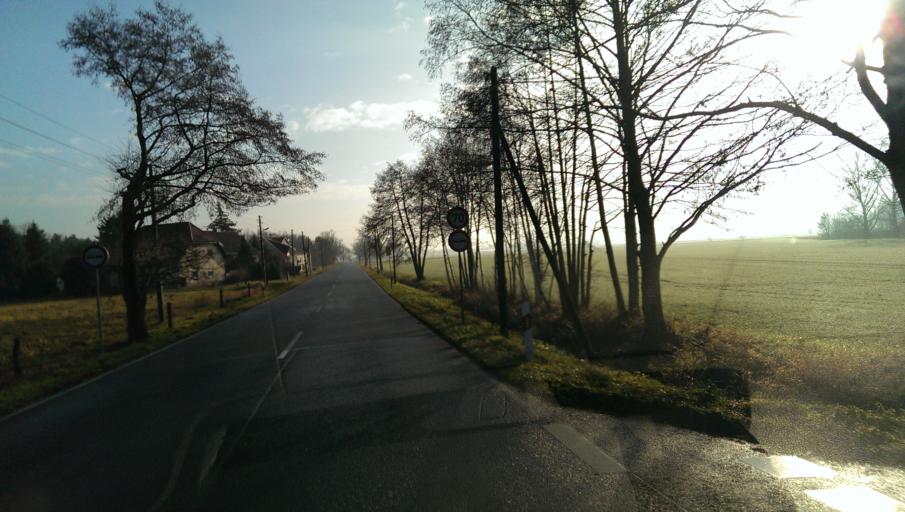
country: DE
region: Brandenburg
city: Schilda
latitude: 51.6260
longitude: 13.3226
